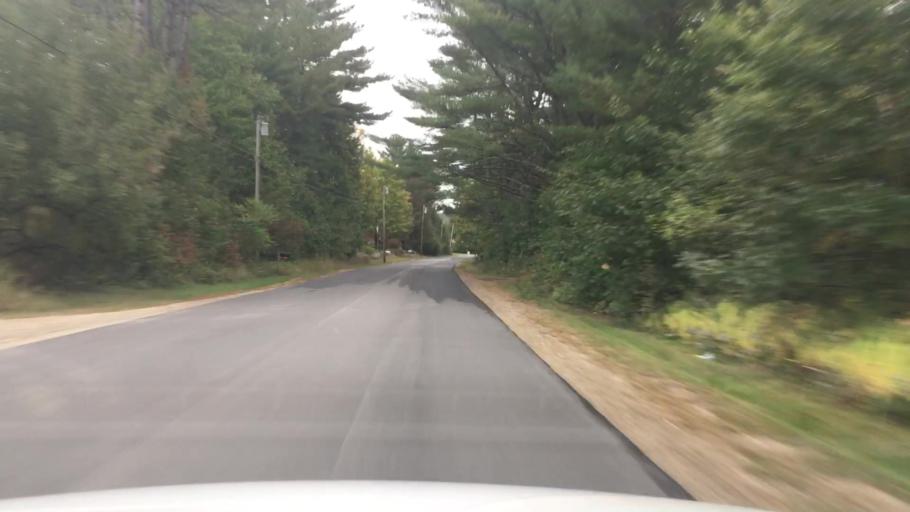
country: US
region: Maine
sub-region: Oxford County
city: Bethel
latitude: 44.4813
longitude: -70.7496
